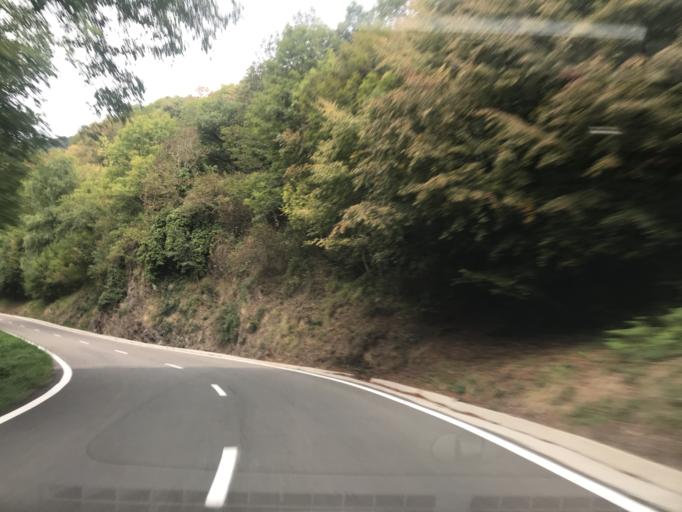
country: ES
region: Catalonia
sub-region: Provincia de Lleida
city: Les
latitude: 42.7790
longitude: 0.6860
